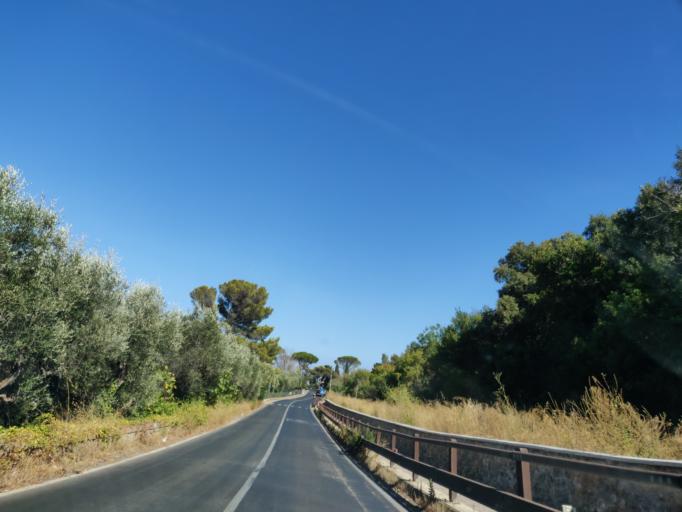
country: IT
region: Tuscany
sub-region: Provincia di Grosseto
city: Monte Argentario
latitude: 42.4347
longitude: 11.1522
